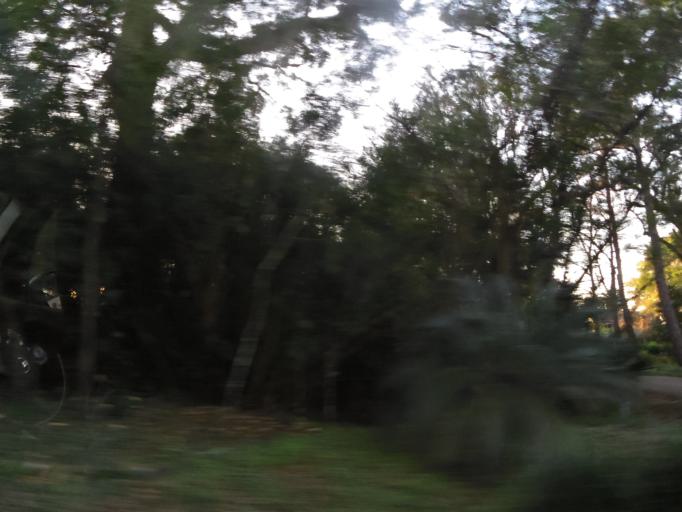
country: US
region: Florida
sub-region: Duval County
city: Jacksonville
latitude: 30.2741
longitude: -81.7062
